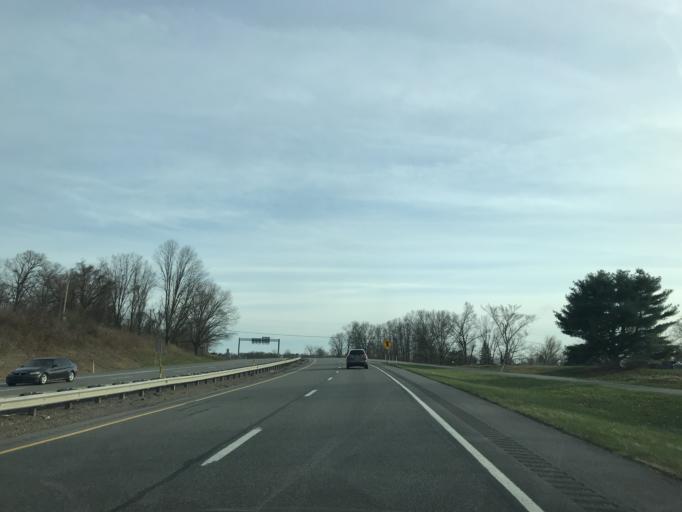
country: US
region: Pennsylvania
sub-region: Union County
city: New Columbia
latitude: 41.0468
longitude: -76.8414
